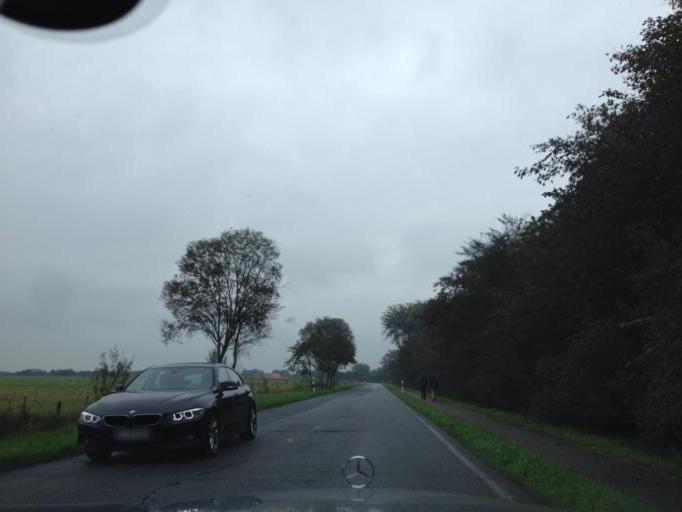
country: DE
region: Schleswig-Holstein
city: Wrixum
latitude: 54.6928
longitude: 8.5348
